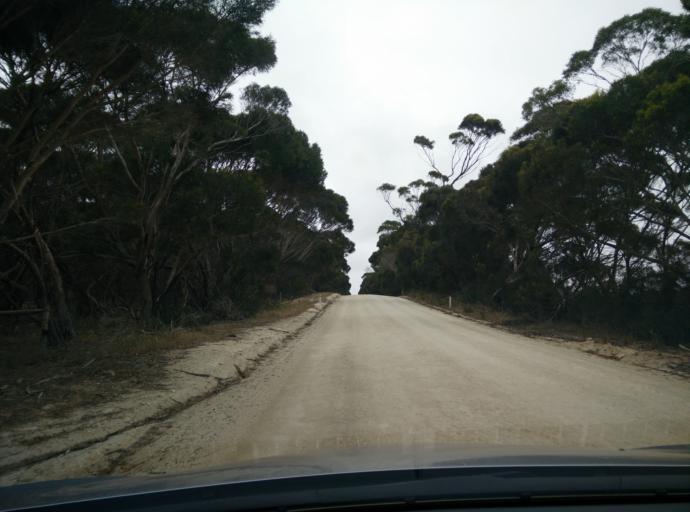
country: AU
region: South Australia
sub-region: Kangaroo Island
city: Kingscote
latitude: -35.8319
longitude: 137.5612
